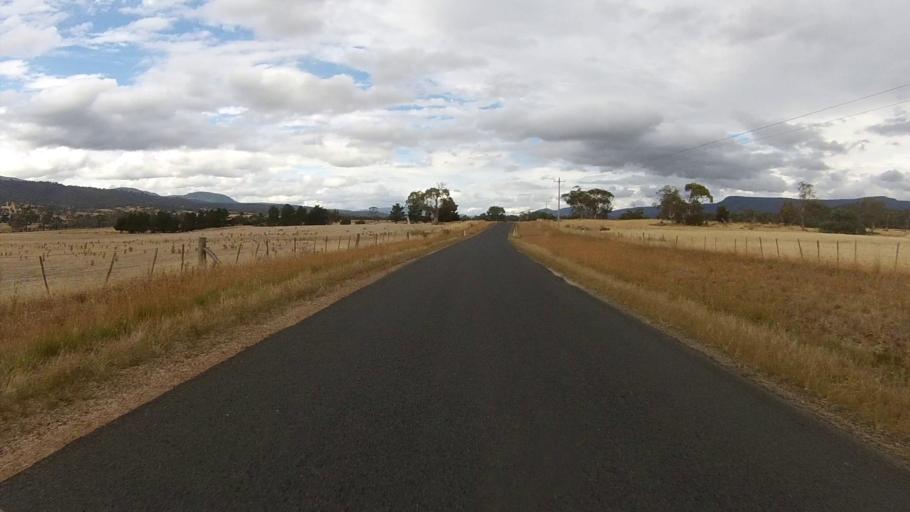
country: AU
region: Tasmania
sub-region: Northern Midlands
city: Evandale
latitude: -41.8237
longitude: 147.8155
